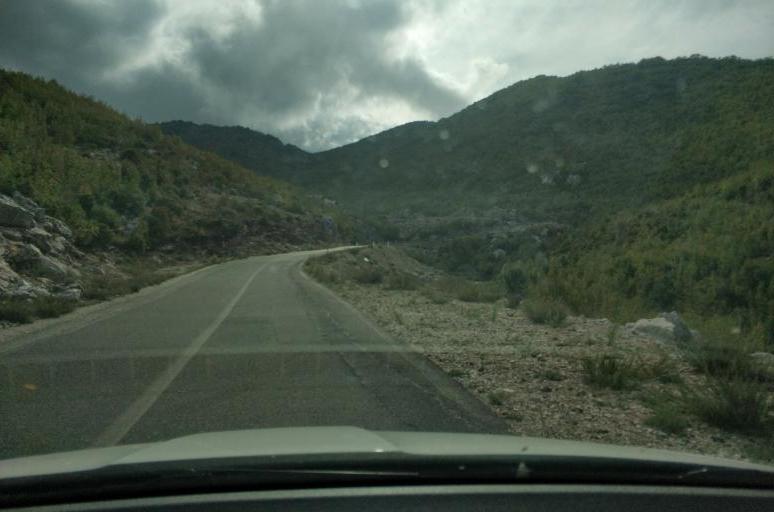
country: AL
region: Durres
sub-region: Rrethi i Krujes
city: Kruje
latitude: 41.5282
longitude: 19.7968
